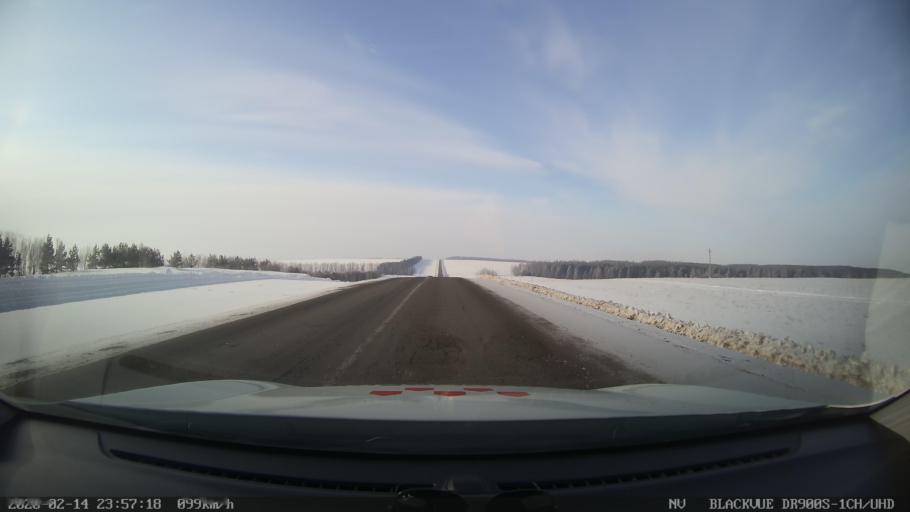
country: RU
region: Tatarstan
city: Kuybyshevskiy Zaton
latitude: 55.3329
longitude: 49.1129
